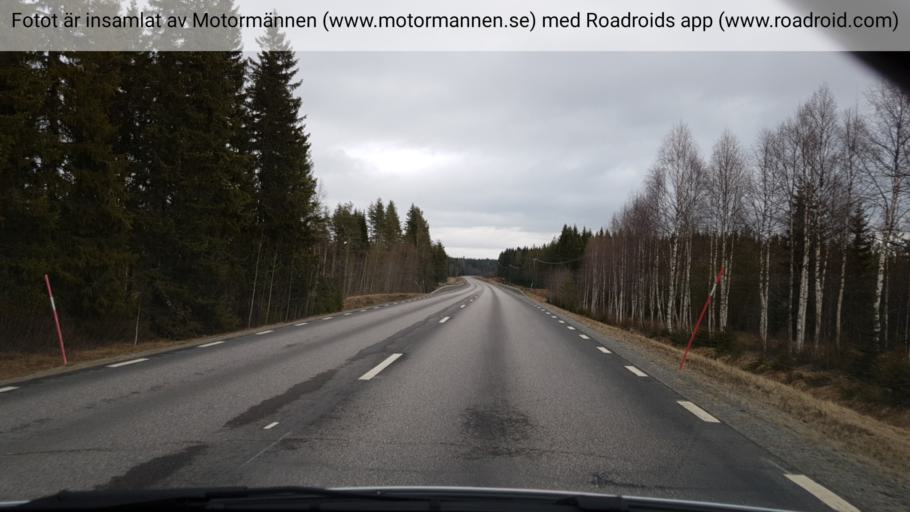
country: SE
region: Vaesterbotten
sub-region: Vannas Kommun
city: Vaennaes
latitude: 63.9208
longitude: 19.6209
